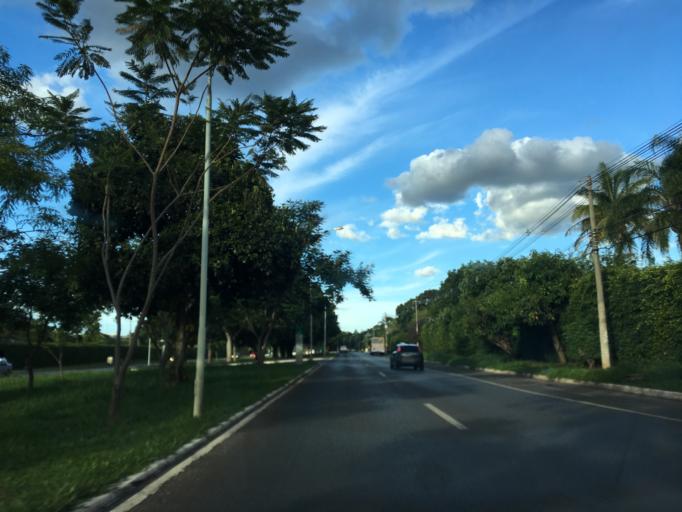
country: BR
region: Federal District
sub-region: Brasilia
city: Brasilia
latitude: -15.8539
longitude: -47.9135
